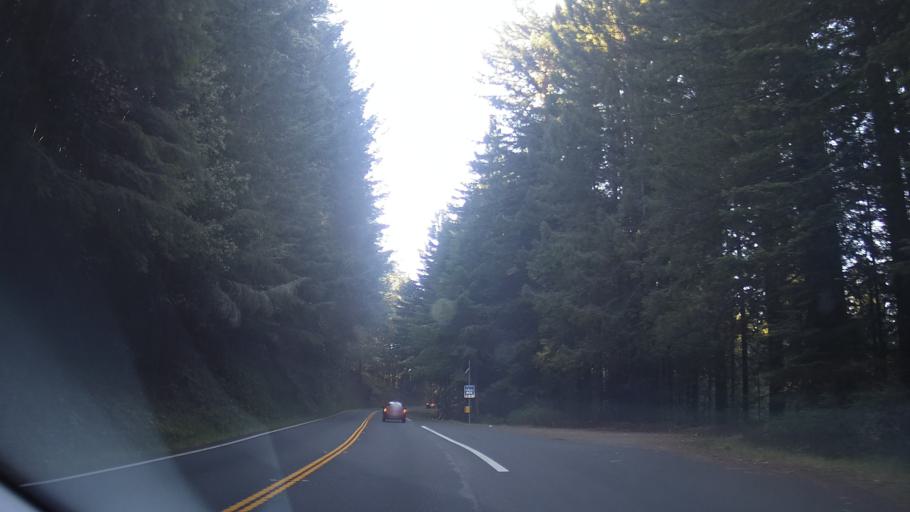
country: US
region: California
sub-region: Mendocino County
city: Fort Bragg
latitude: 39.3672
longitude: -123.6784
